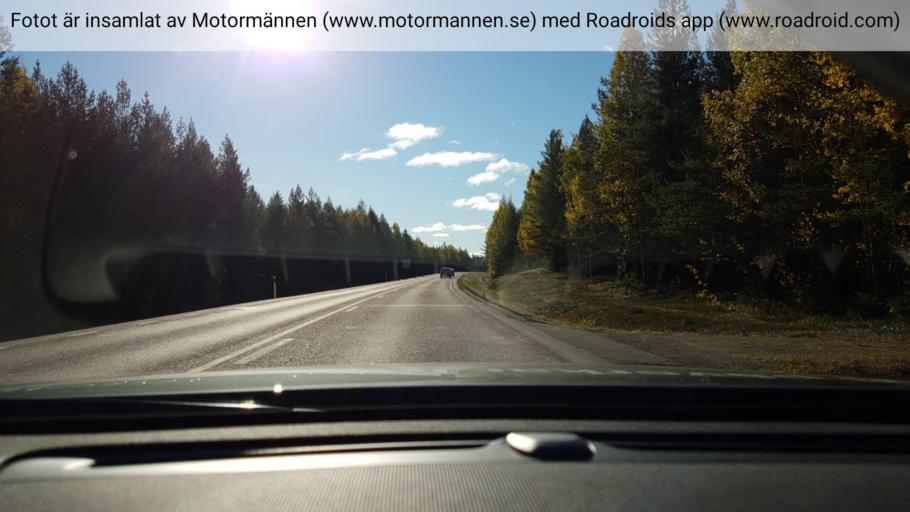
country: SE
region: Vaesterbotten
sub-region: Skelleftea Kommun
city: Burea
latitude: 64.6300
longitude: 21.1762
